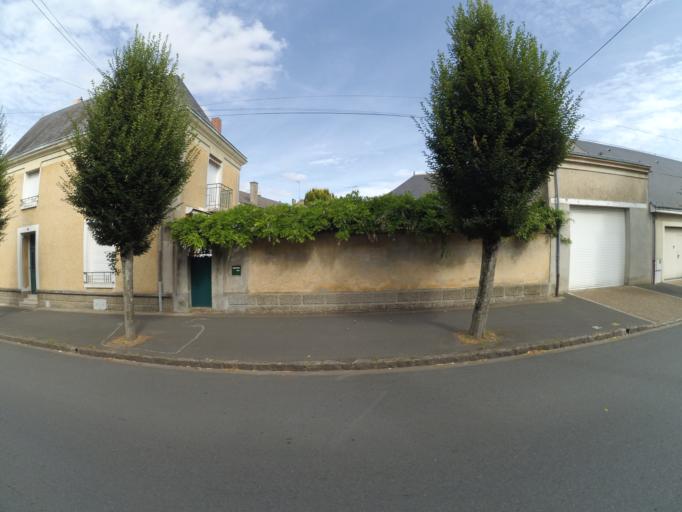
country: FR
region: Pays de la Loire
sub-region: Departement de Maine-et-Loire
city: Doue-la-Fontaine
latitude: 47.1915
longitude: -0.2764
